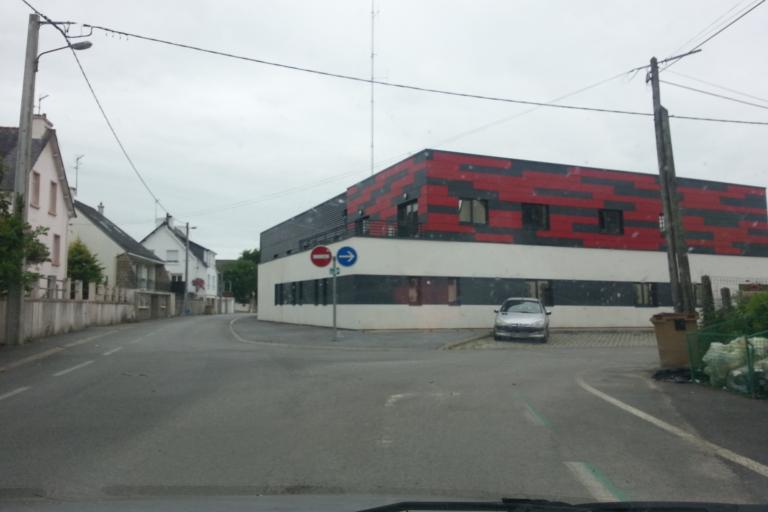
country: FR
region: Brittany
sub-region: Departement du Morbihan
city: Le Faouet
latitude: 48.0356
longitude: -3.4947
